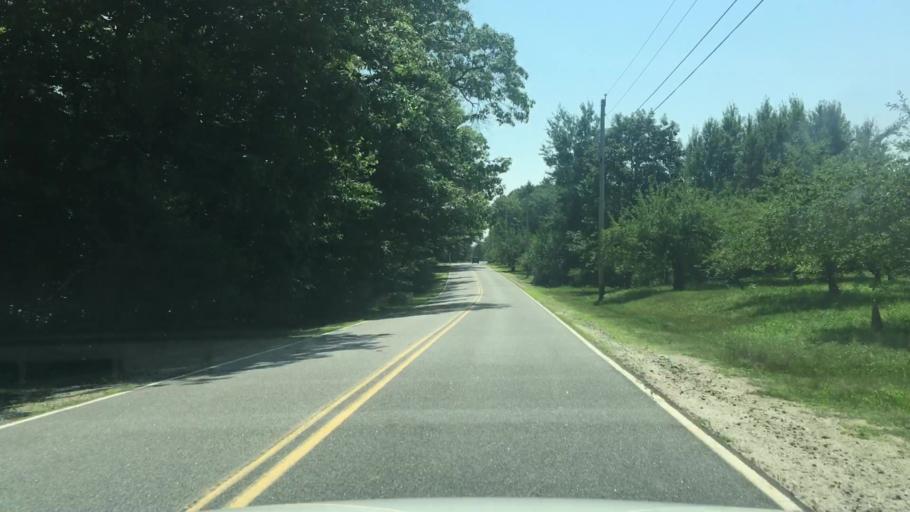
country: US
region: Maine
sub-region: Cumberland County
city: Cumberland Center
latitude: 43.8356
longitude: -70.3045
